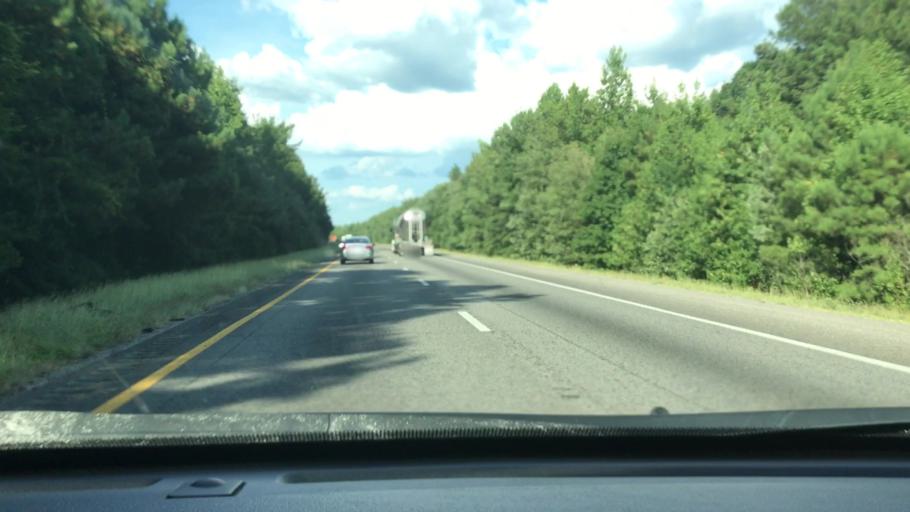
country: US
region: South Carolina
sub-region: Dillon County
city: Latta
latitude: 34.3191
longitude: -79.5893
